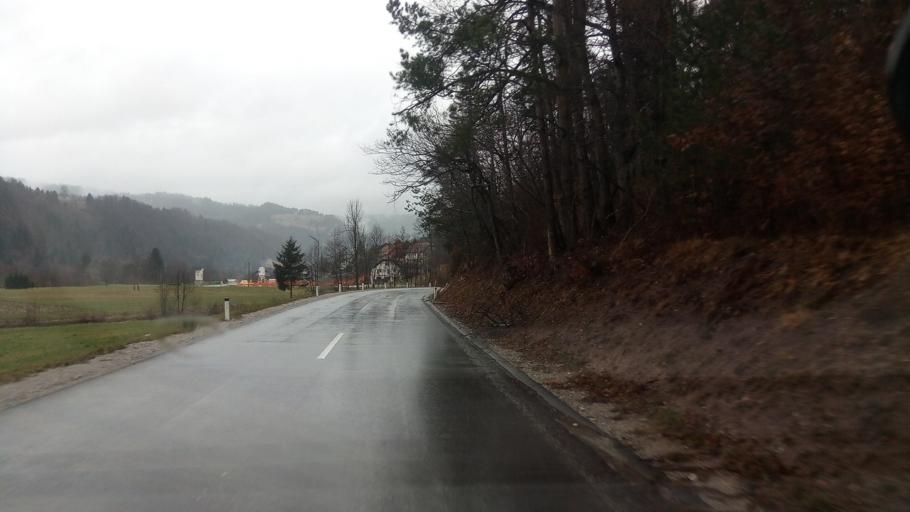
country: SI
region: Vrhnika
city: Vrhnika
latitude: 45.9960
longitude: 14.2440
